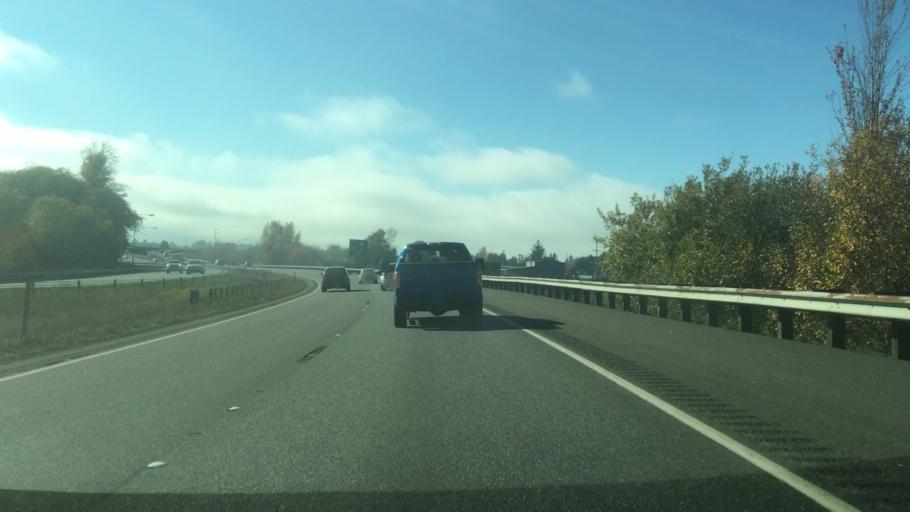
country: US
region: Washington
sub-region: Grays Harbor County
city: Montesano
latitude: 46.9787
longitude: -123.5929
